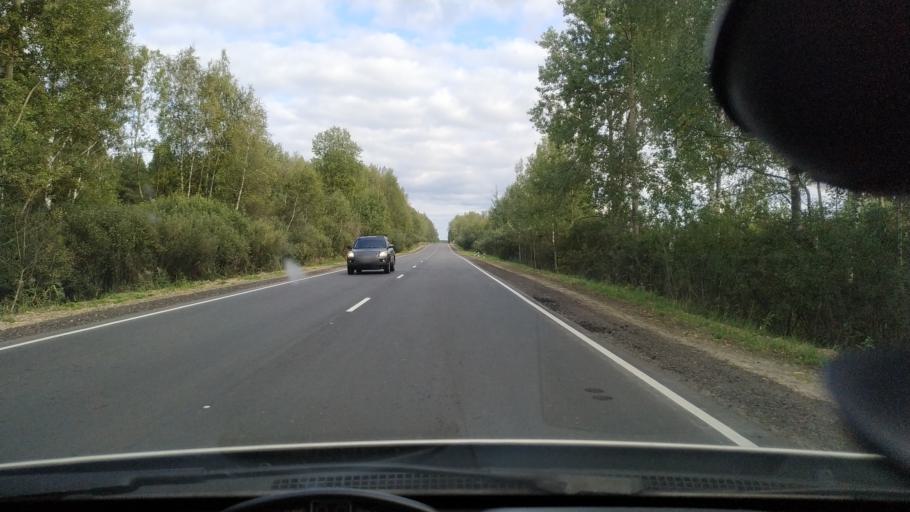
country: RU
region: Moskovskaya
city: Likino-Dulevo
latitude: 55.7279
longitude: 39.0267
